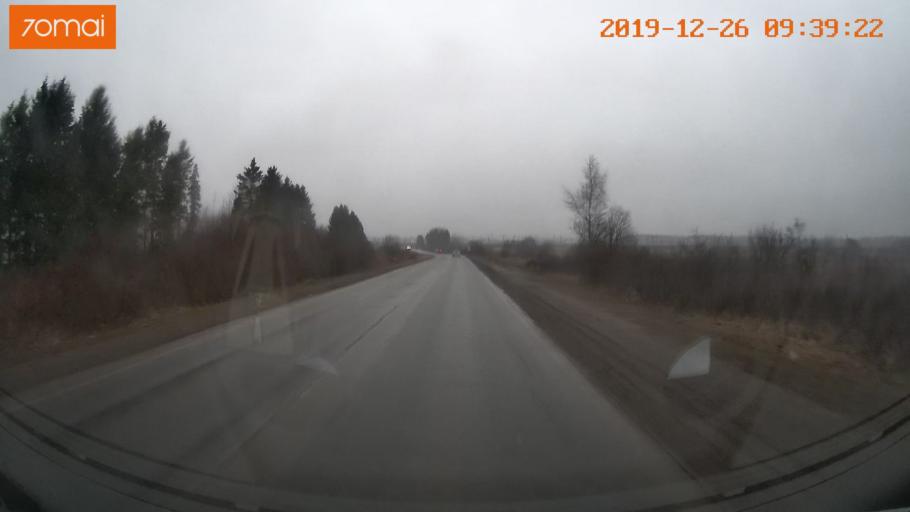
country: RU
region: Vologda
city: Vologda
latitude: 59.1536
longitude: 40.0262
